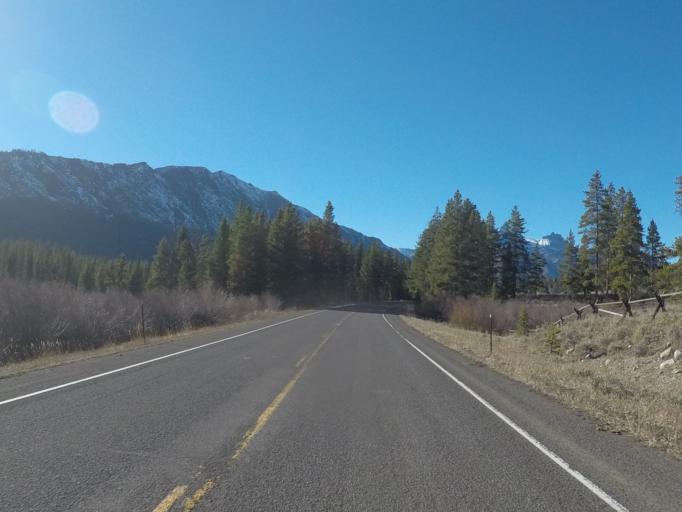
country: US
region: Montana
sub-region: Carbon County
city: Red Lodge
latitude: 44.9344
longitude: -109.7548
